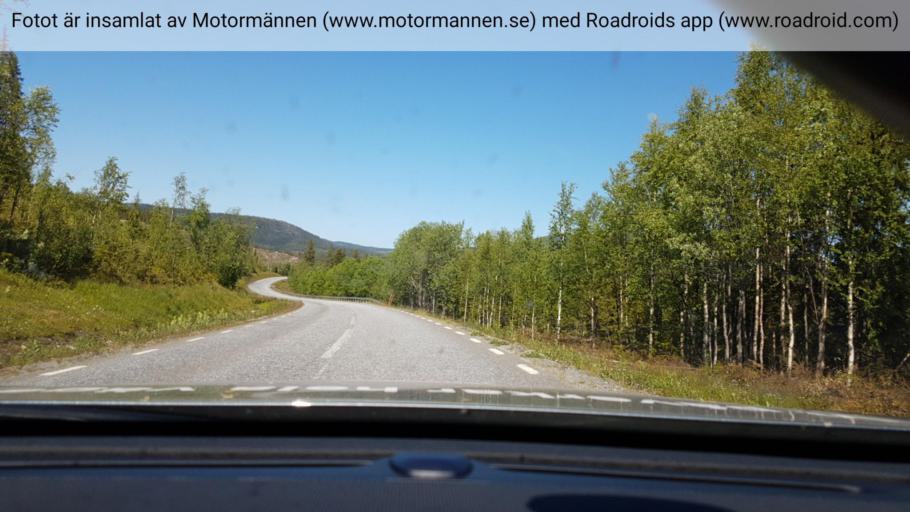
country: SE
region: Vaesterbotten
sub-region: Vilhelmina Kommun
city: Sjoberg
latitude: 64.9155
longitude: 15.8719
